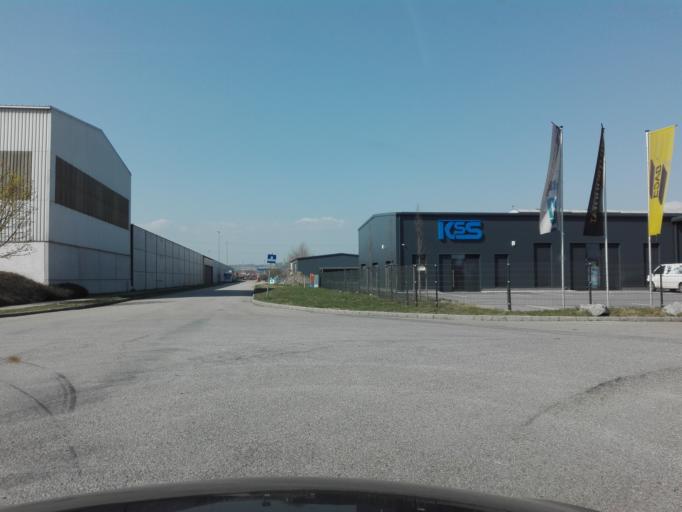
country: AT
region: Lower Austria
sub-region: Politischer Bezirk Amstetten
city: Ennsdorf
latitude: 48.2252
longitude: 14.5090
